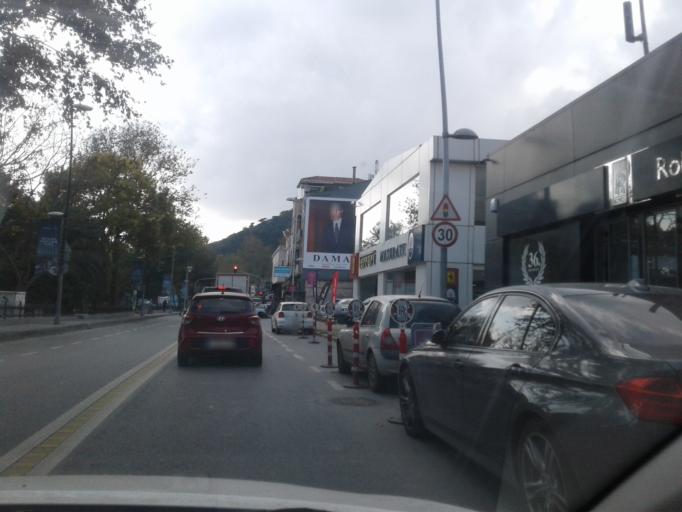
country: TR
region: Istanbul
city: UEskuedar
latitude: 41.0609
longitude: 29.0372
